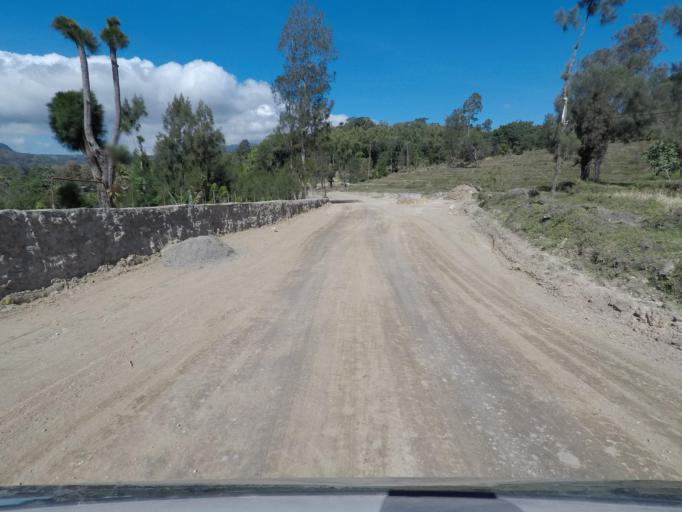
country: TL
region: Baucau
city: Venilale
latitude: -8.6545
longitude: 126.3705
